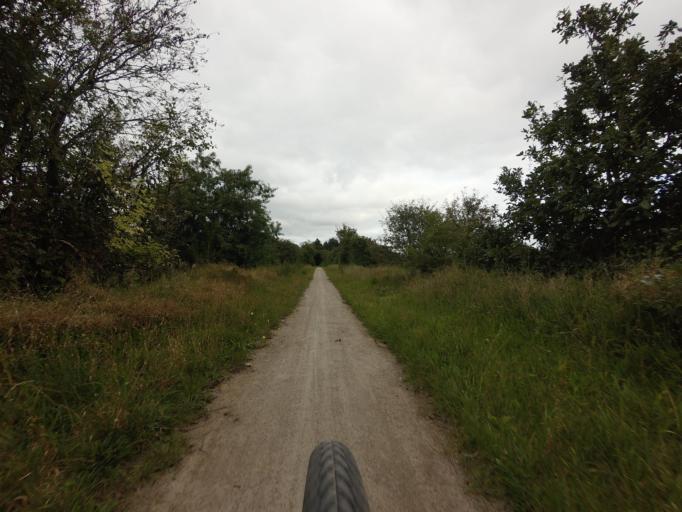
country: DK
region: South Denmark
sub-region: Billund Kommune
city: Grindsted
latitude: 55.8028
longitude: 9.0130
